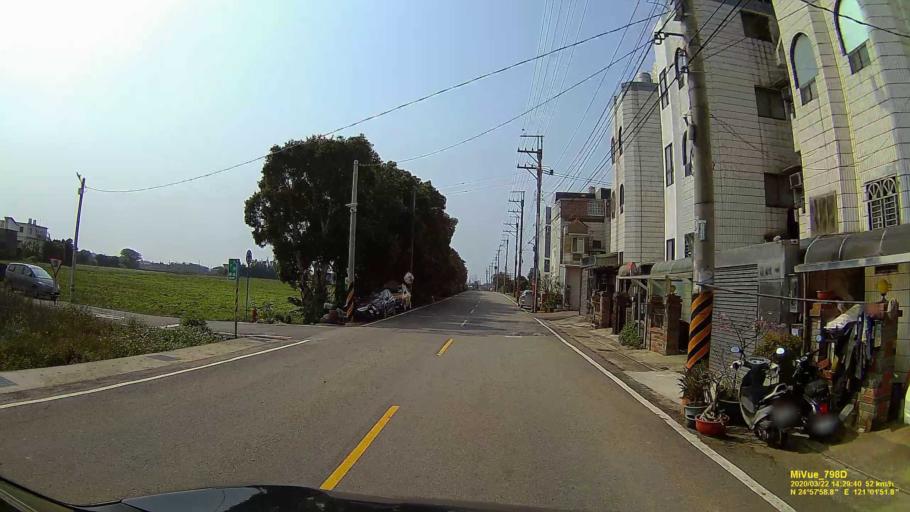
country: TW
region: Taiwan
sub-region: Hsinchu
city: Zhubei
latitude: 24.9664
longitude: 121.0309
